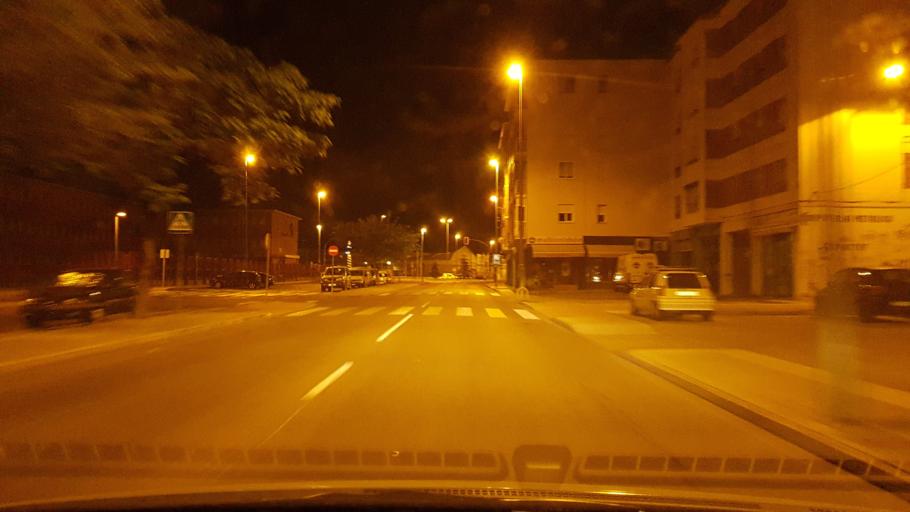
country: ES
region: Castille and Leon
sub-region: Provincia de Zamora
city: Zamora
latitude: 41.5097
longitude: -5.7476
